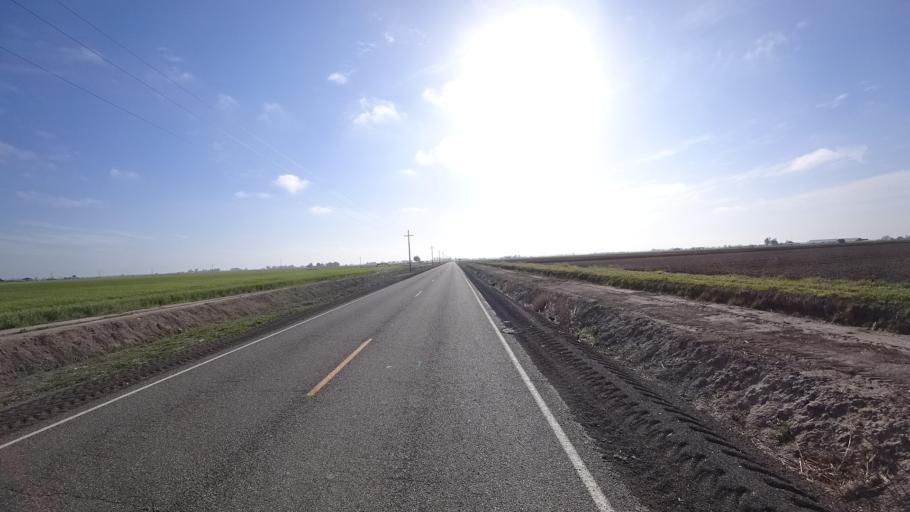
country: US
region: California
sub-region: Glenn County
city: Willows
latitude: 39.5828
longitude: -122.0928
